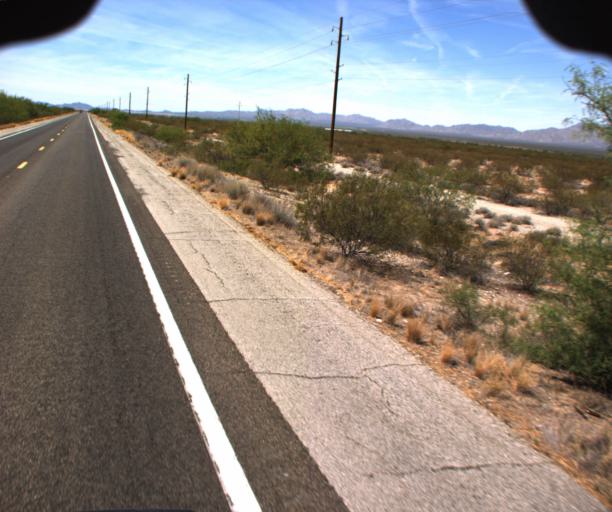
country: US
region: Arizona
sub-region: La Paz County
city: Salome
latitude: 33.8526
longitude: -113.4441
